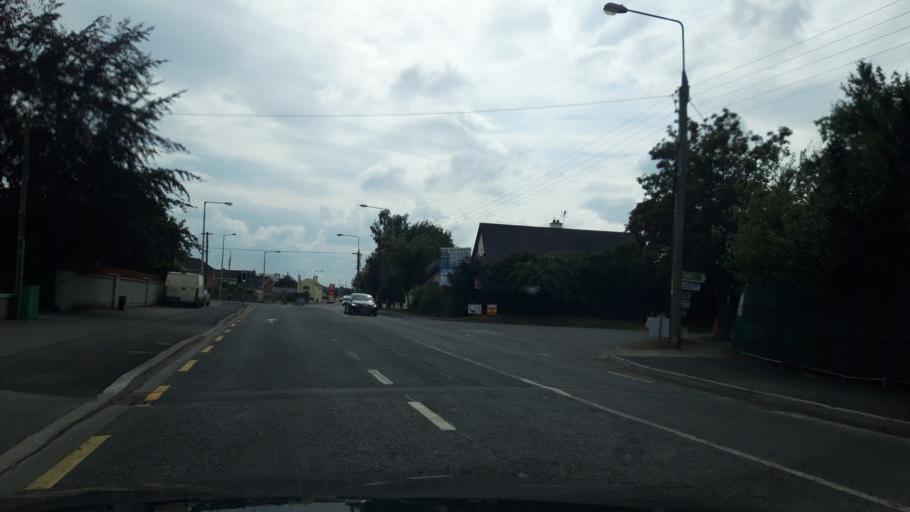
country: IE
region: Leinster
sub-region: Kildare
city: Athy
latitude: 52.9887
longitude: -6.9940
